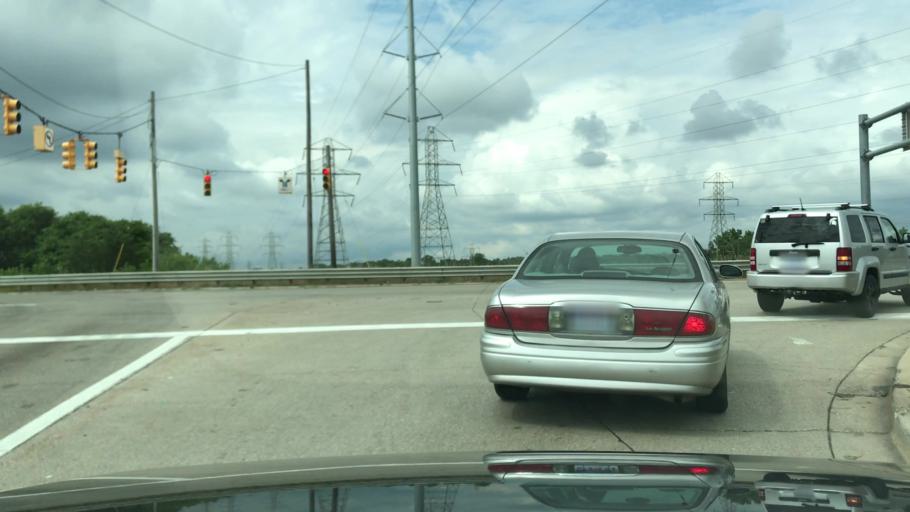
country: US
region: Michigan
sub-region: Kent County
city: Wyoming
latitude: 42.9130
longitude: -85.6766
